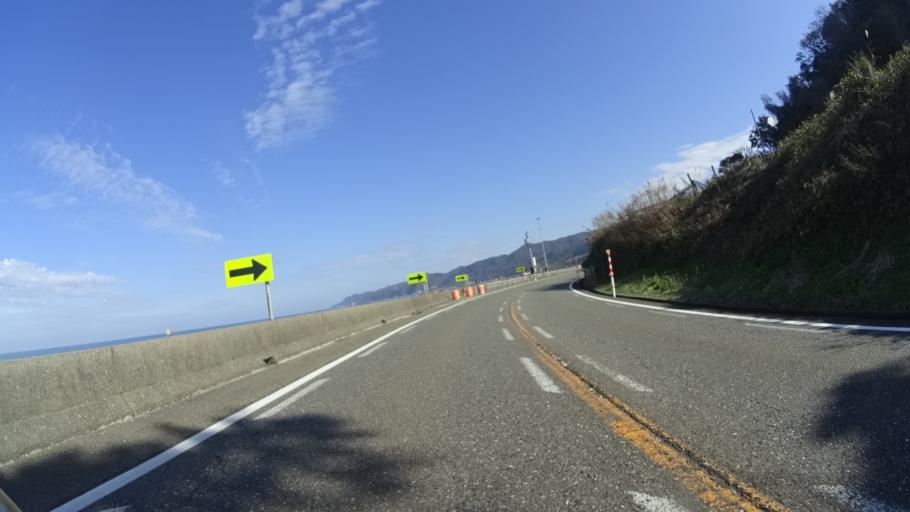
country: JP
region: Niigata
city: Itoigawa
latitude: 37.1153
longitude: 138.0123
